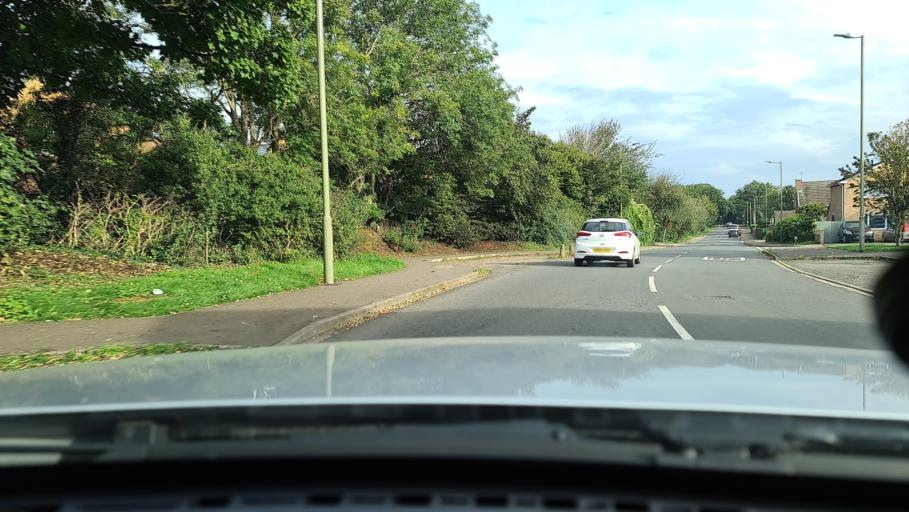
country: GB
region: England
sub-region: Oxfordshire
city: Hanwell
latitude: 52.0680
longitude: -1.3684
